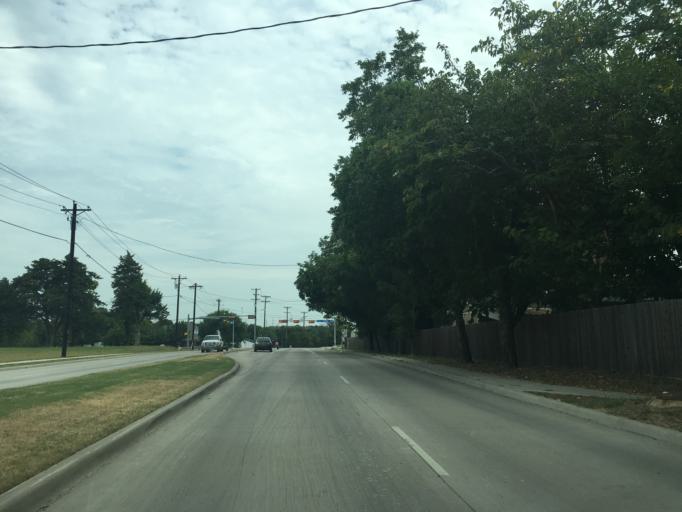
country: US
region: Texas
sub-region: Collin County
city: Wylie
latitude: 33.0046
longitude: -96.5220
